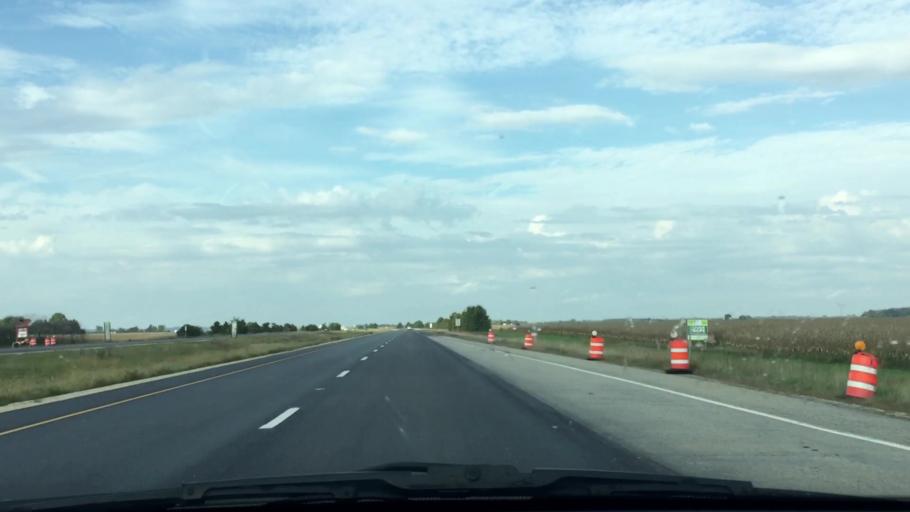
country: US
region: Illinois
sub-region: Whiteside County
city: Erie
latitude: 41.6891
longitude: -90.1040
